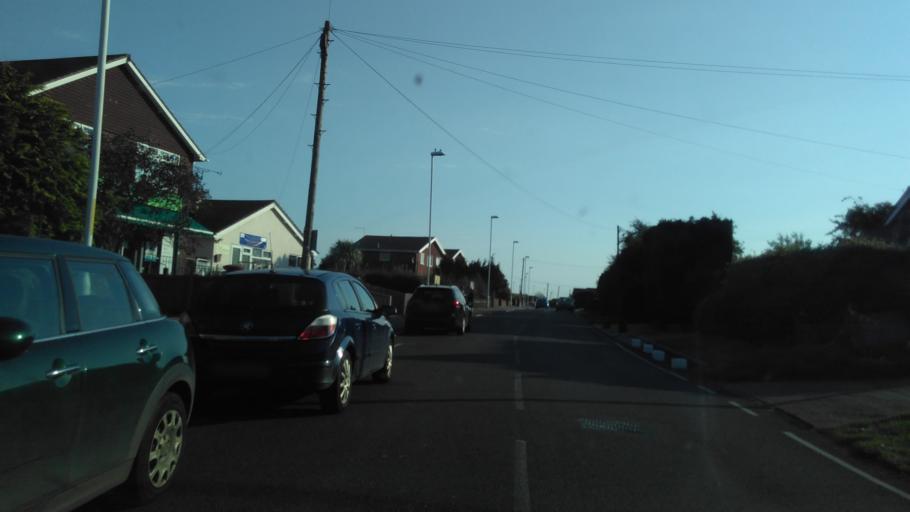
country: GB
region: England
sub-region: Kent
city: Whitstable
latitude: 51.3437
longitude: 1.0009
